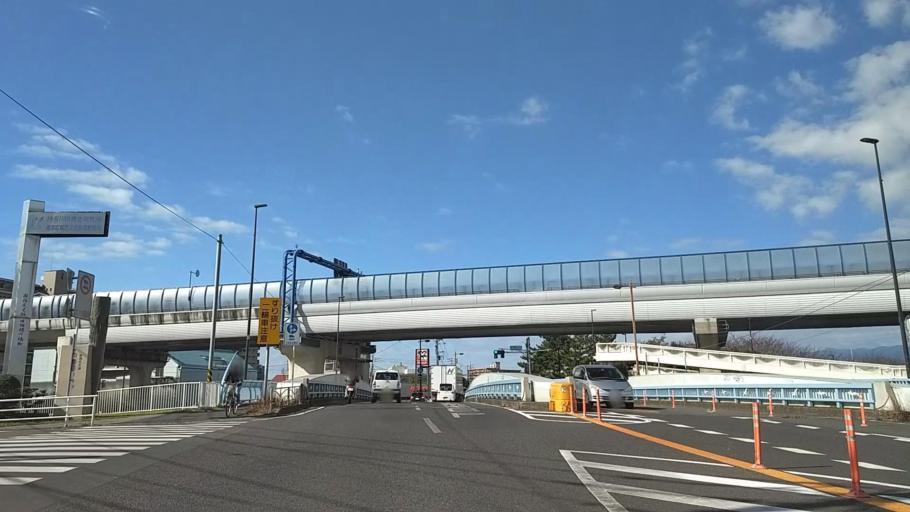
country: JP
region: Kanagawa
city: Chigasaki
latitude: 35.3326
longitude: 139.3847
